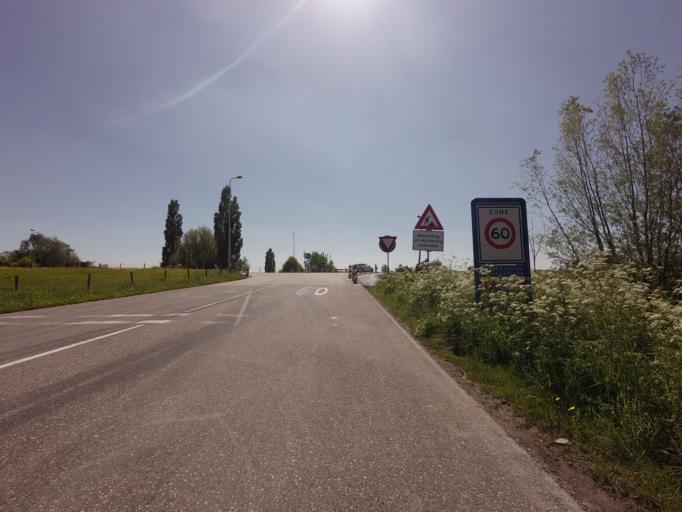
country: NL
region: South Holland
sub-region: Molenwaard
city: Liesveld
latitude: 51.9170
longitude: 4.7877
